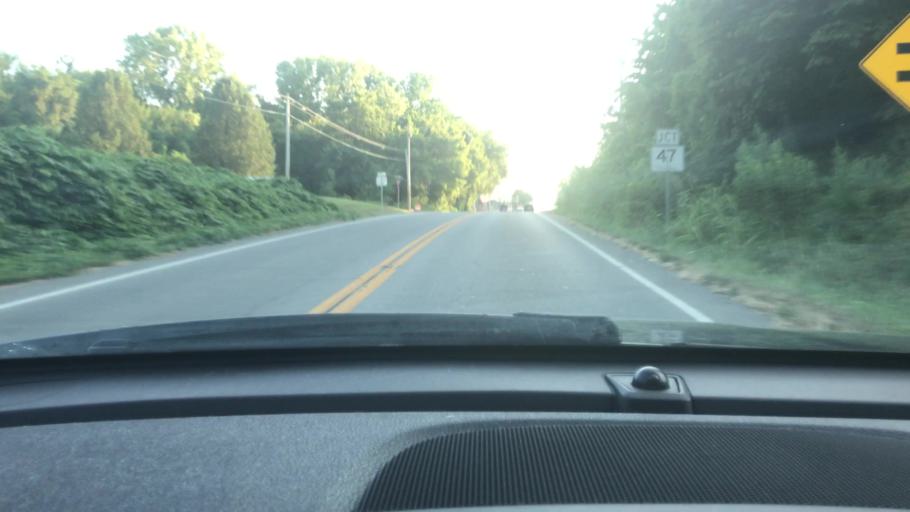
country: US
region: Tennessee
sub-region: Dickson County
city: Charlotte
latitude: 36.1727
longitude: -87.3452
